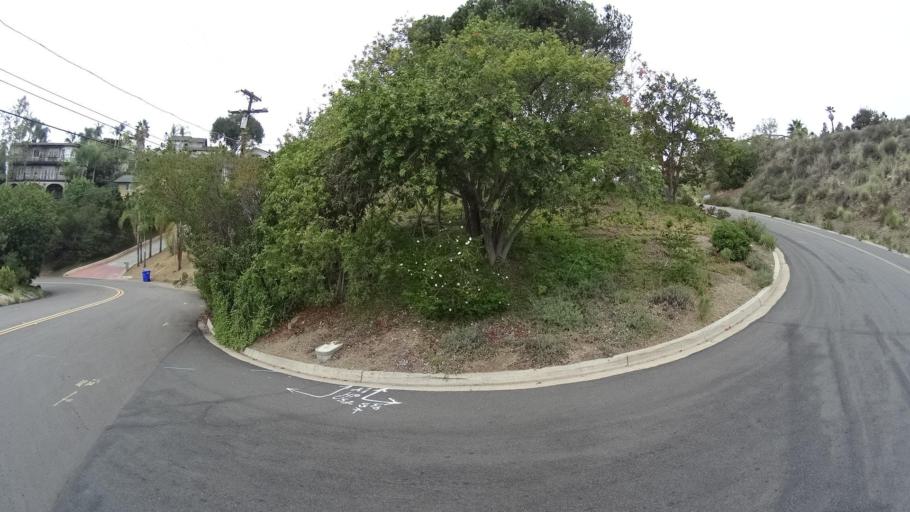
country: US
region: California
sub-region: San Diego County
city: Spring Valley
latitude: 32.7587
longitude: -116.9887
